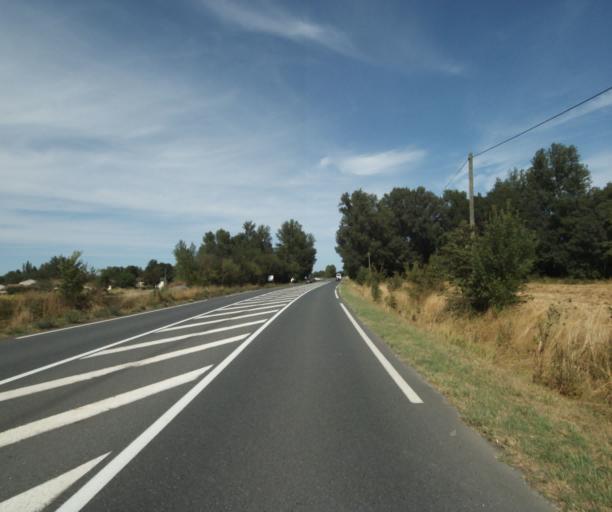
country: FR
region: Midi-Pyrenees
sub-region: Departement du Tarn
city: Soual
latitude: 43.5184
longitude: 2.0703
